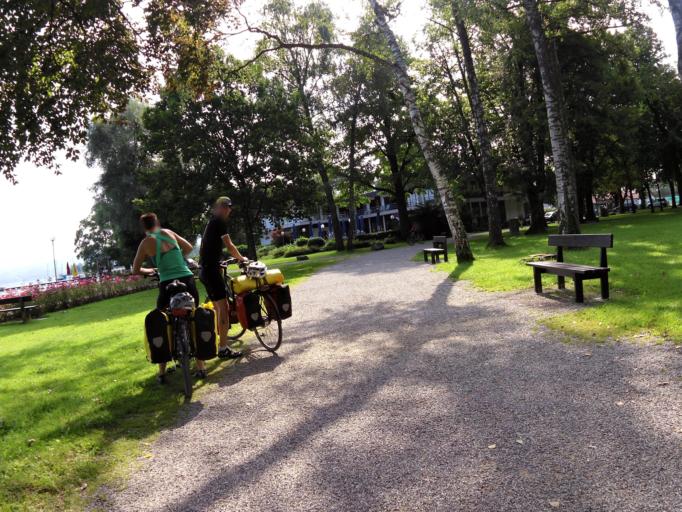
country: DE
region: Bavaria
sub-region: Upper Bavaria
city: Diessen am Ammersee
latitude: 47.9490
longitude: 11.1103
